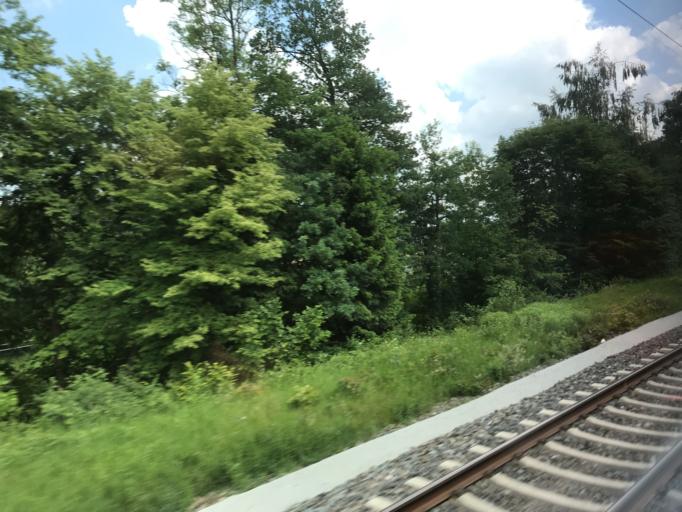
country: DE
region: Bavaria
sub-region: Swabia
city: Dinkelscherben
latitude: 48.3797
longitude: 10.5540
